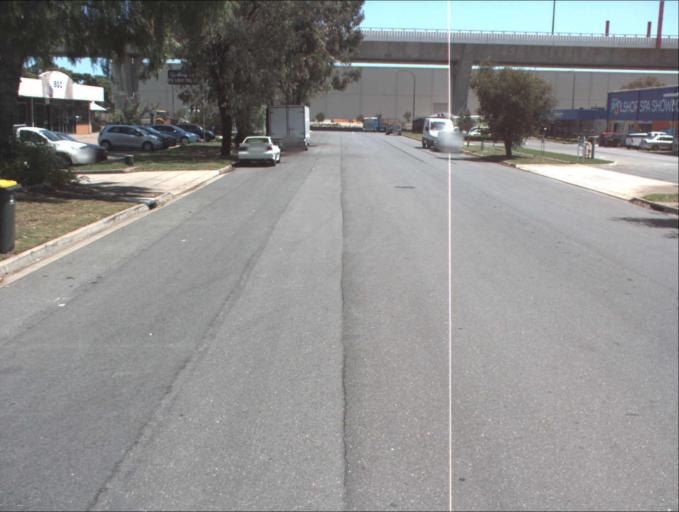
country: AU
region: South Australia
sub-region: Charles Sturt
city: Woodville North
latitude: -34.8533
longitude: 138.5667
